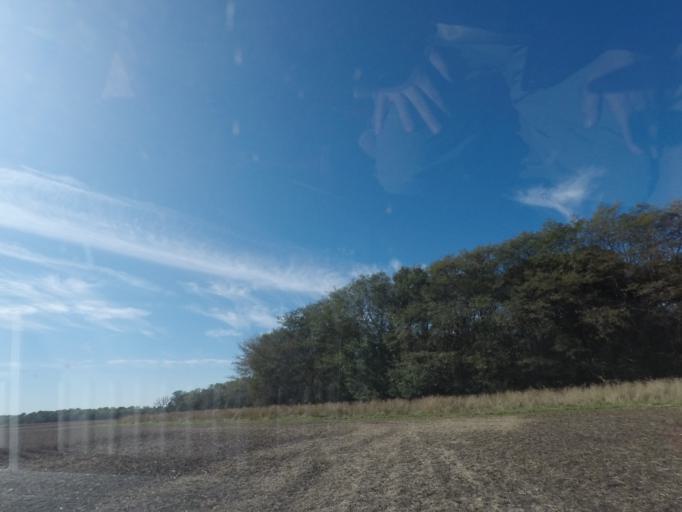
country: US
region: Iowa
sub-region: Story County
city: Nevada
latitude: 42.0321
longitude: -93.3751
